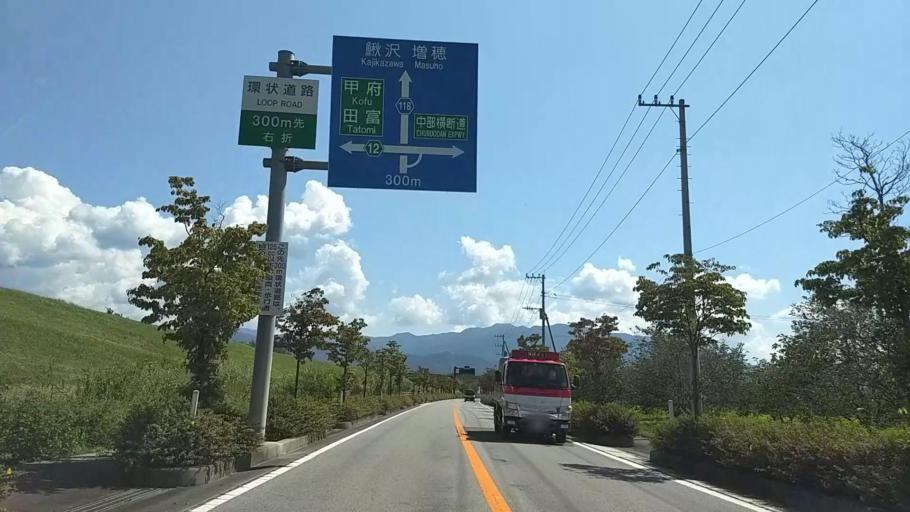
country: JP
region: Yamanashi
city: Ryuo
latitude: 35.6106
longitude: 138.5036
